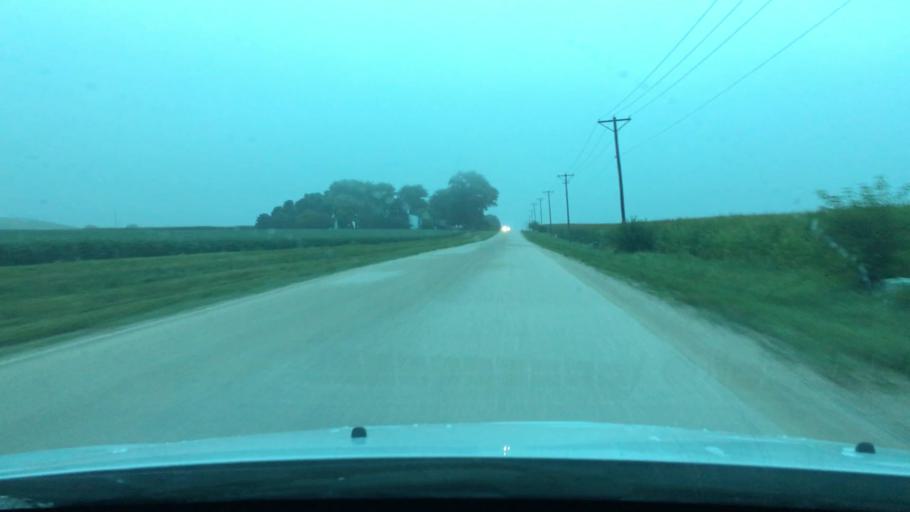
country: US
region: Illinois
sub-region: Ogle County
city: Rochelle
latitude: 41.9201
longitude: -89.0082
